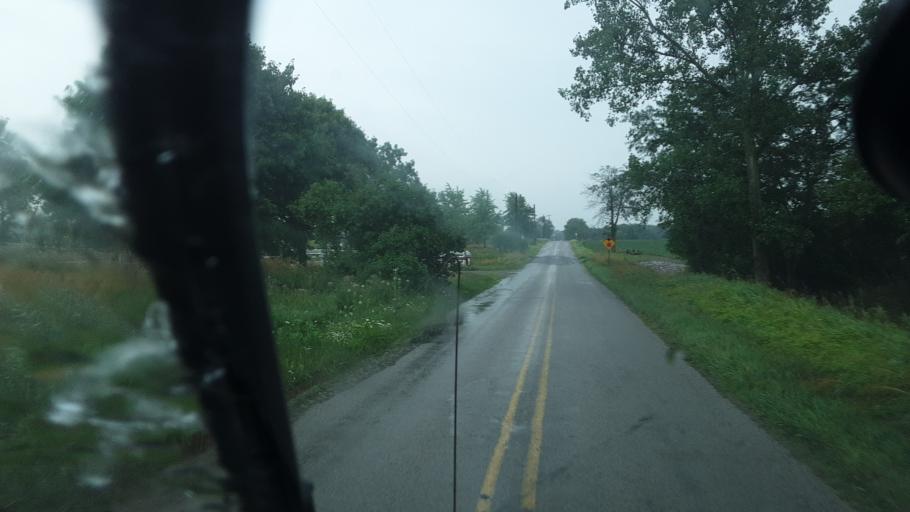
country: US
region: Indiana
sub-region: DeKalb County
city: Butler
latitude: 41.4403
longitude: -84.8139
